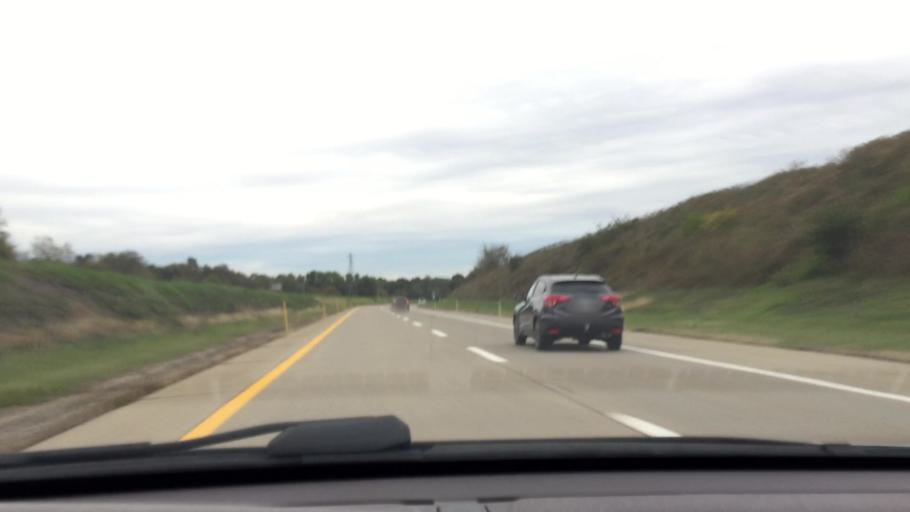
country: US
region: Pennsylvania
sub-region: Lawrence County
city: Oakland
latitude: 40.9715
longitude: -80.4004
